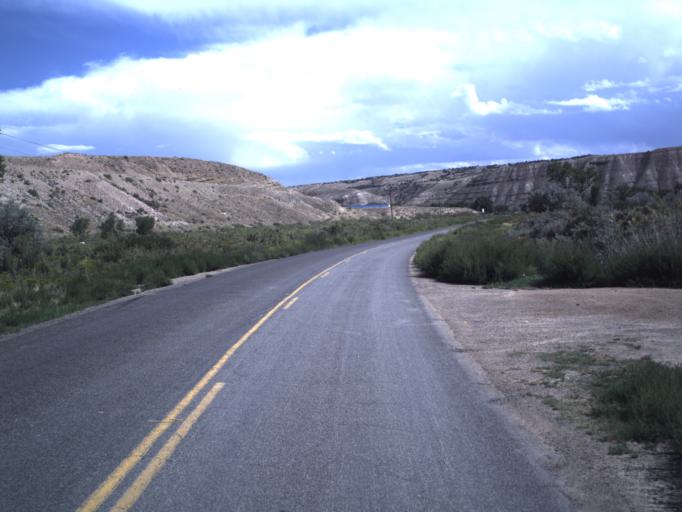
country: US
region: Utah
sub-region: Duchesne County
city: Duchesne
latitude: 40.1696
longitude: -110.4180
